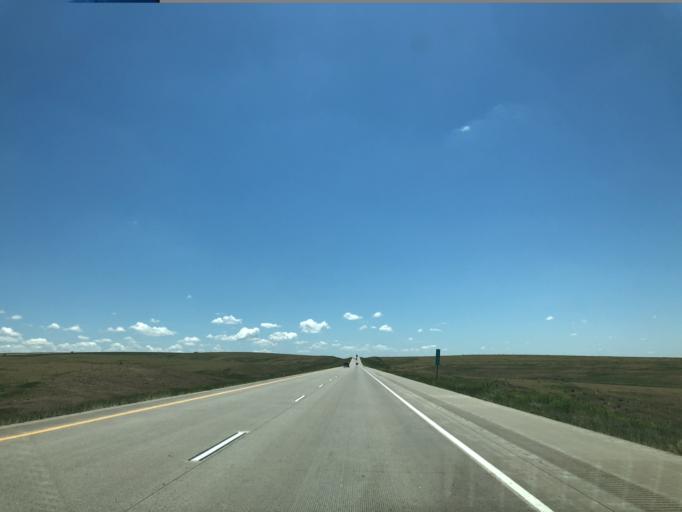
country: US
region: Colorado
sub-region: Lincoln County
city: Limon
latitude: 39.4024
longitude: -103.9002
